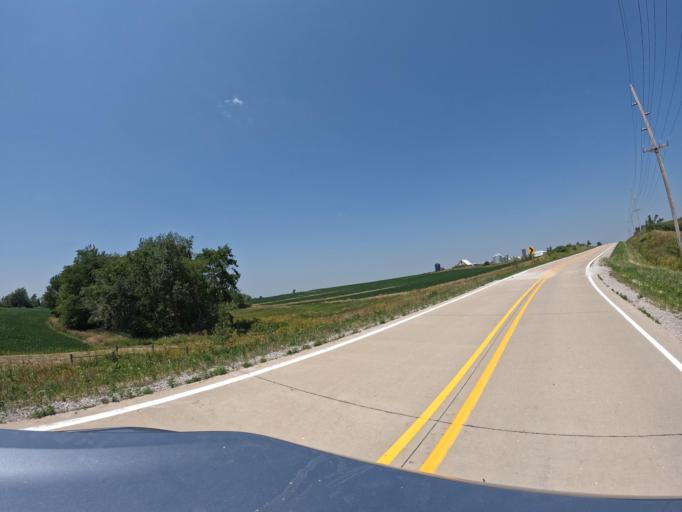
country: US
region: Iowa
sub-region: Keokuk County
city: Sigourney
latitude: 41.2768
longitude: -92.1806
